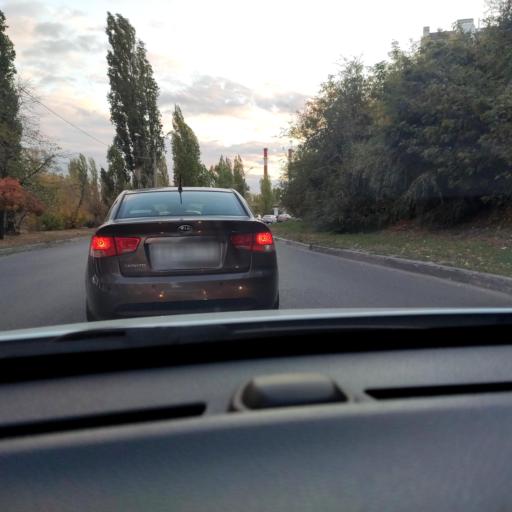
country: RU
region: Voronezj
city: Voronezh
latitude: 51.6626
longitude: 39.2190
